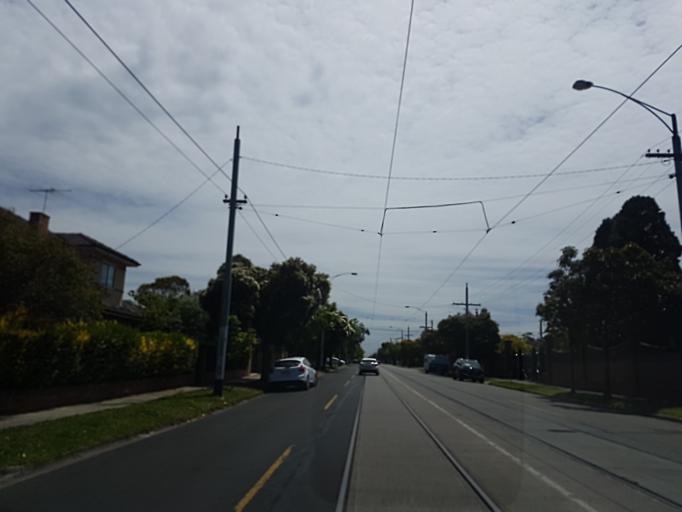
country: AU
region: Victoria
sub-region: Bayside
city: Brighton East
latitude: -37.8985
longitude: 145.0198
